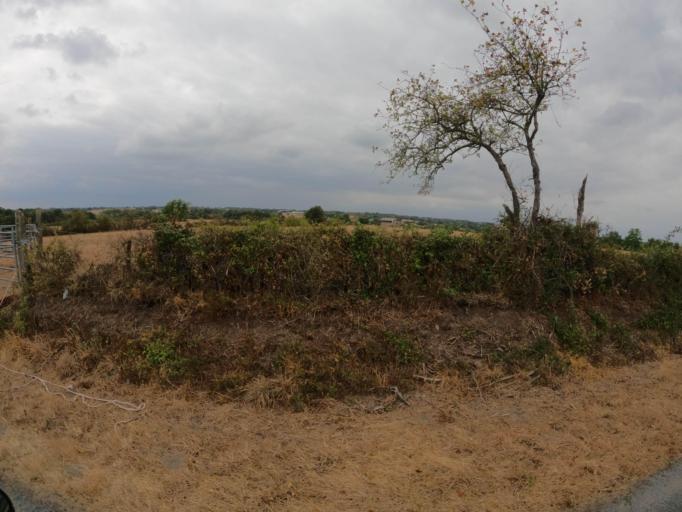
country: FR
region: Pays de la Loire
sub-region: Departement de la Vendee
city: Tiffauges
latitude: 47.0011
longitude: -1.1080
